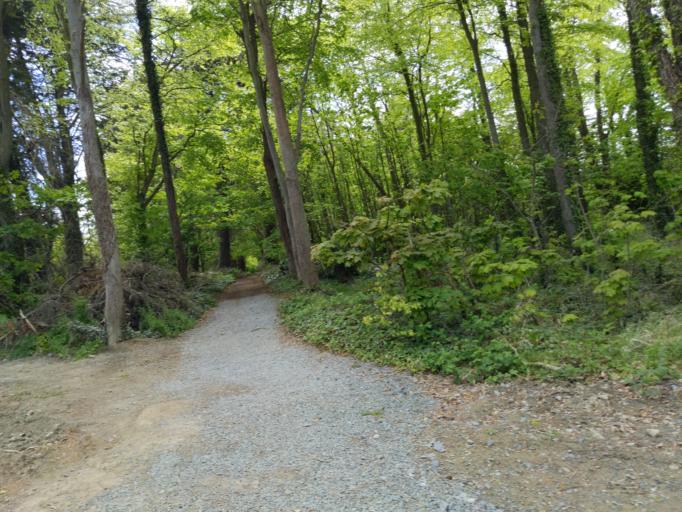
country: IE
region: Leinster
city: Portraine
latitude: 53.4856
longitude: -6.1158
